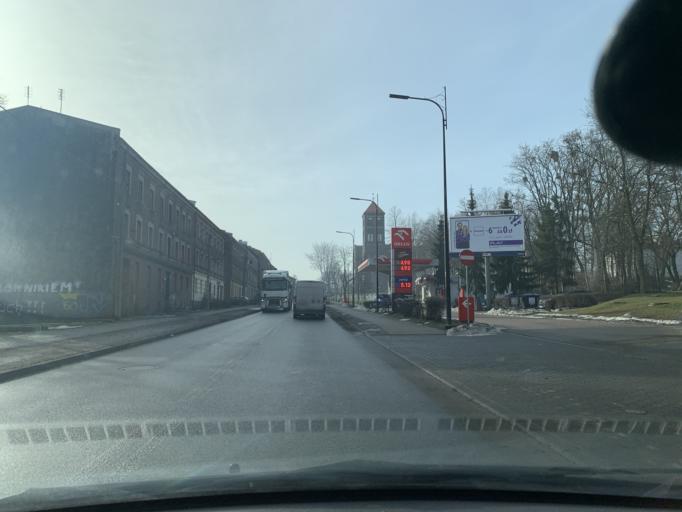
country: PL
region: Silesian Voivodeship
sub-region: Ruda Slaska
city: Ruda Slaska
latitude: 50.3218
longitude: 18.8572
